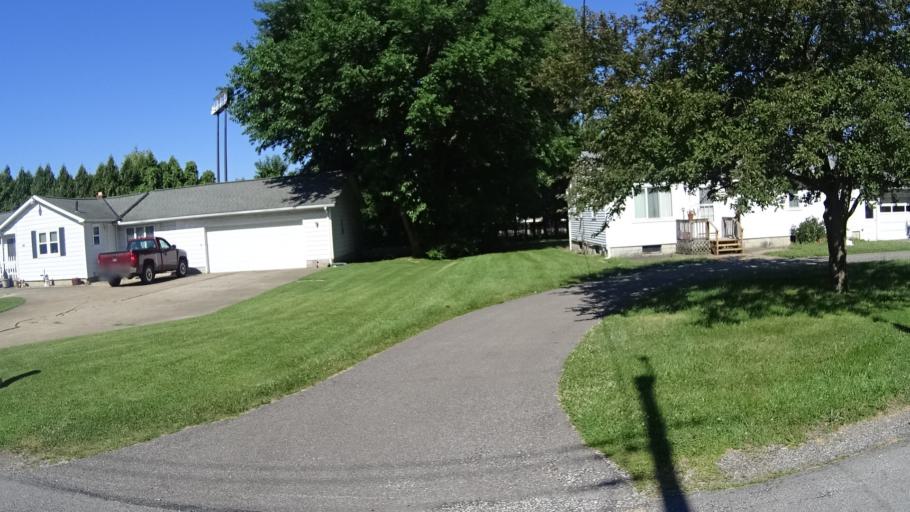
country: US
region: Ohio
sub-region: Erie County
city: Sandusky
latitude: 41.3979
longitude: -82.6516
